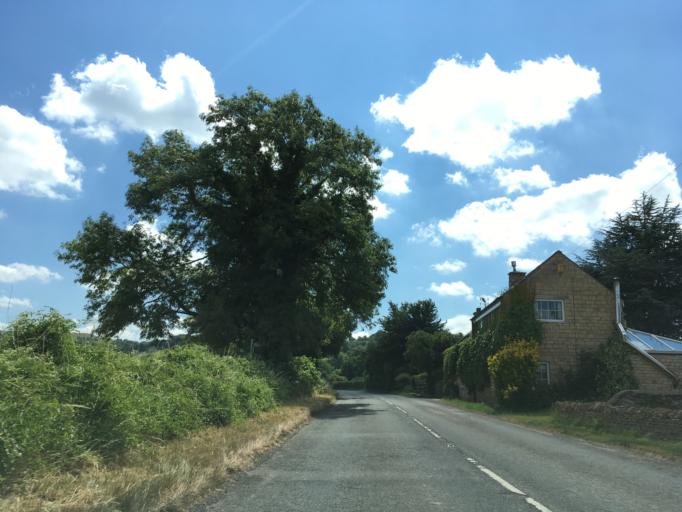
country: GB
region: England
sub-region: Gloucestershire
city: Painswick
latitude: 51.8203
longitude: -2.2083
